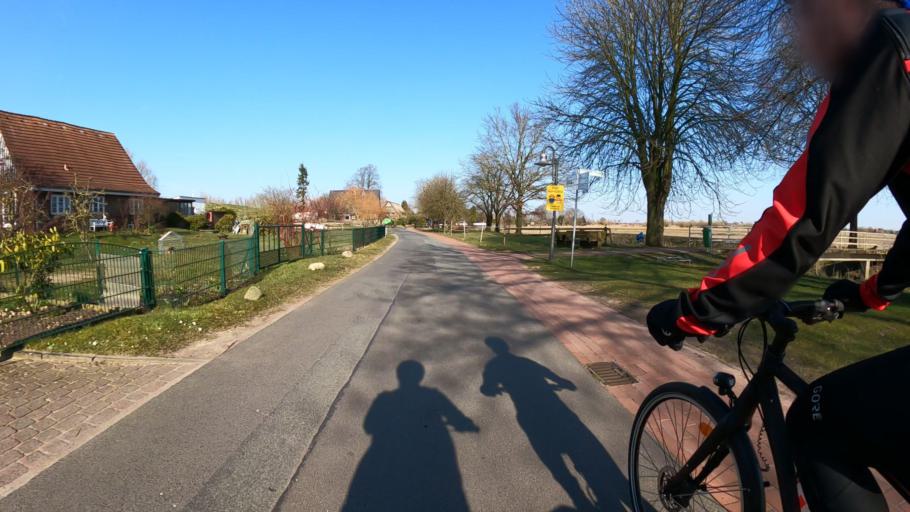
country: DE
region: Schleswig-Holstein
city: Seester
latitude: 53.7234
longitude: 9.5889
